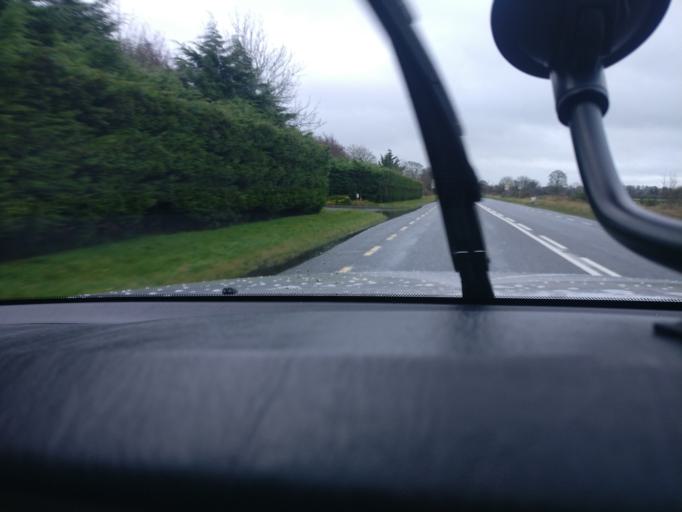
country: IE
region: Leinster
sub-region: An Mhi
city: Longwood
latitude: 53.4259
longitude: -6.8993
